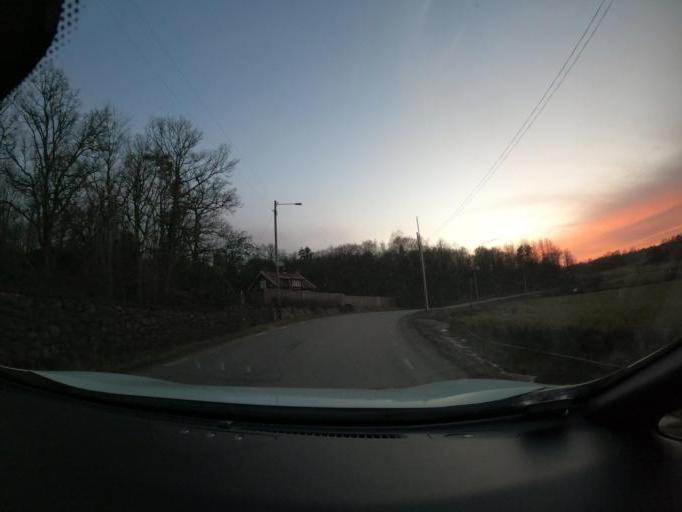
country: SE
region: Vaestra Goetaland
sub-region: Molndal
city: Lindome
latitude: 57.6018
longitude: 12.1164
